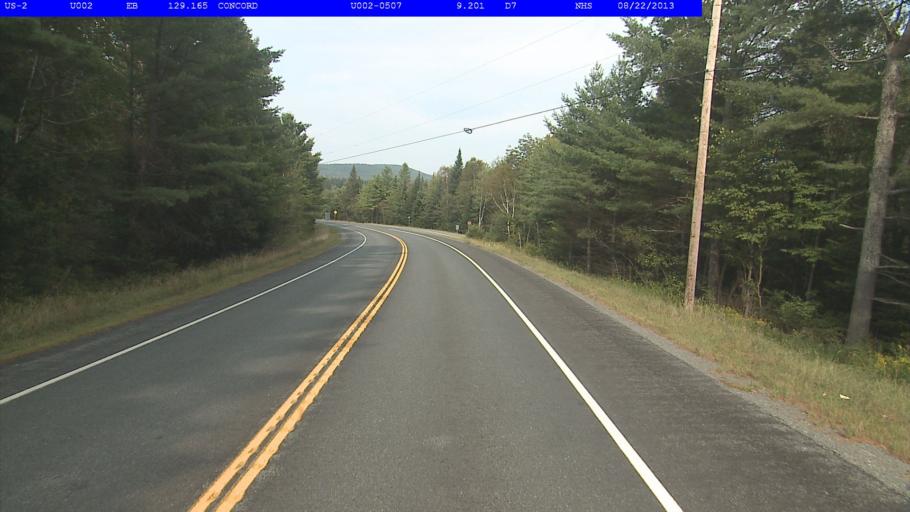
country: US
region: New Hampshire
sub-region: Grafton County
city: Littleton
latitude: 44.4504
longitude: -71.7929
